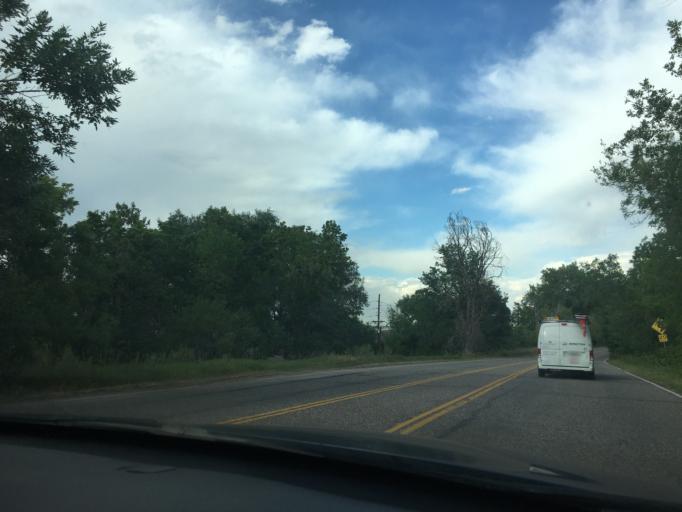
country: US
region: Colorado
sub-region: Jefferson County
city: Golden
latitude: 39.7657
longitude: -105.1932
